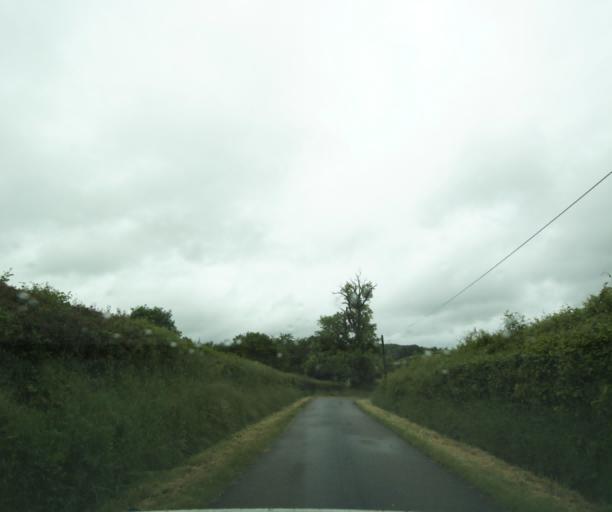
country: FR
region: Bourgogne
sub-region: Departement de Saone-et-Loire
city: Saint-Vallier
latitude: 46.4941
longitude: 4.4544
